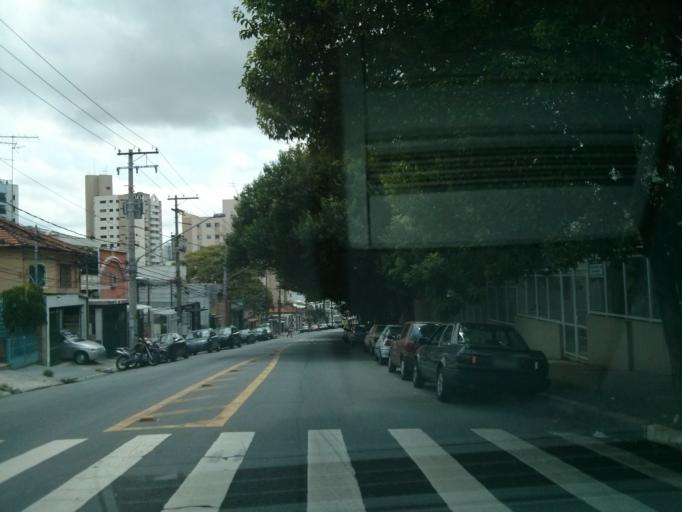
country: BR
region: Sao Paulo
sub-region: Sao Paulo
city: Sao Paulo
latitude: -23.6134
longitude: -46.6230
